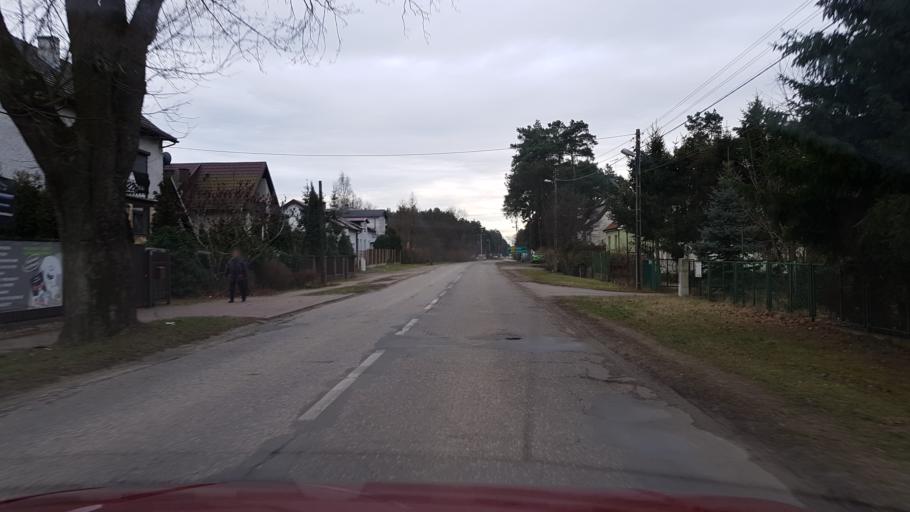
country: PL
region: West Pomeranian Voivodeship
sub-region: Powiat policki
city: Dobra
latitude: 53.5362
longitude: 14.4670
